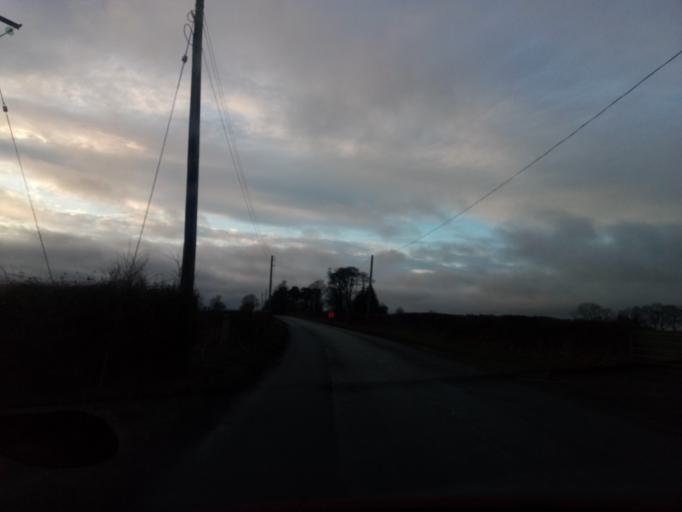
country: GB
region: England
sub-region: Northumberland
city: Meldon
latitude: 55.1330
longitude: -1.7780
